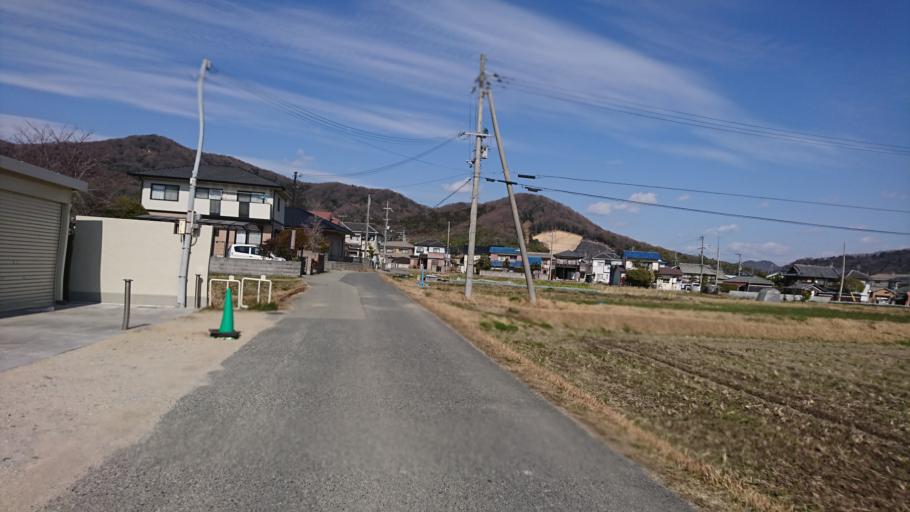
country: JP
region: Hyogo
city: Kakogawacho-honmachi
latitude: 34.8217
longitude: 134.8075
